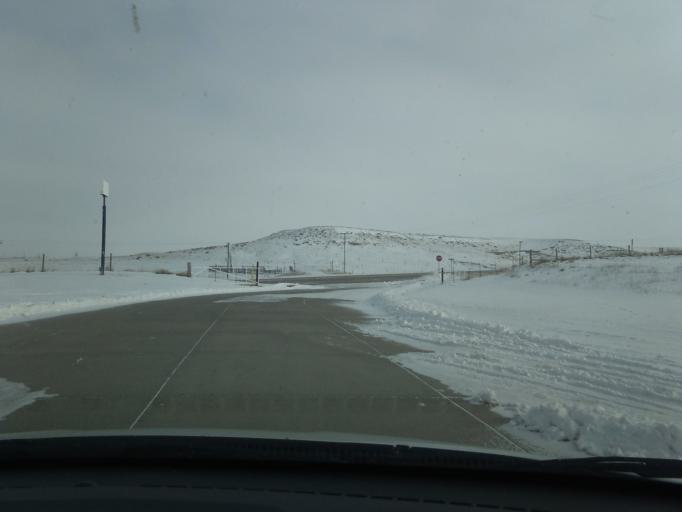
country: US
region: Nebraska
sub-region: Kimball County
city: Kimball
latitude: 41.2141
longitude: -103.6645
